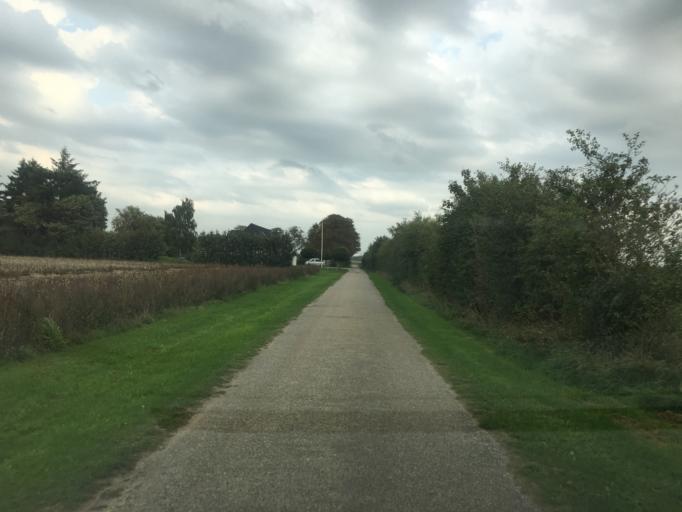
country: DK
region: South Denmark
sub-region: Tonder Kommune
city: Logumkloster
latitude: 55.0026
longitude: 9.0436
